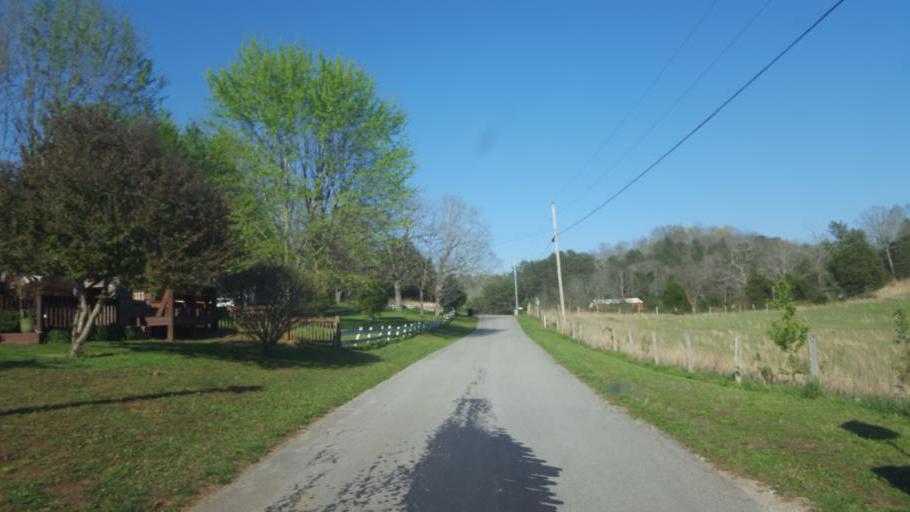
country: US
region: Kentucky
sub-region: Barren County
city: Cave City
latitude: 37.2037
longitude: -86.0240
